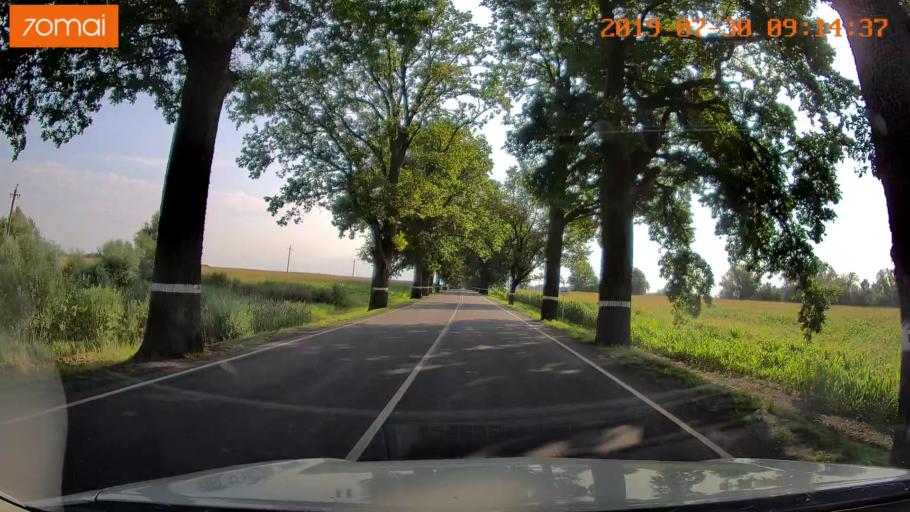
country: RU
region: Kaliningrad
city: Nesterov
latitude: 54.6300
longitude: 22.5222
